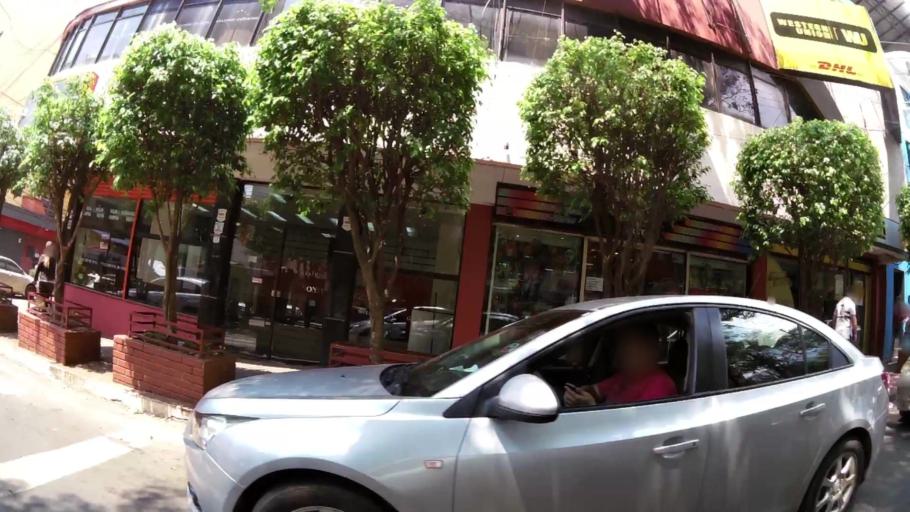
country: PY
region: Alto Parana
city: Ciudad del Este
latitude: -25.5108
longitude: -54.6123
